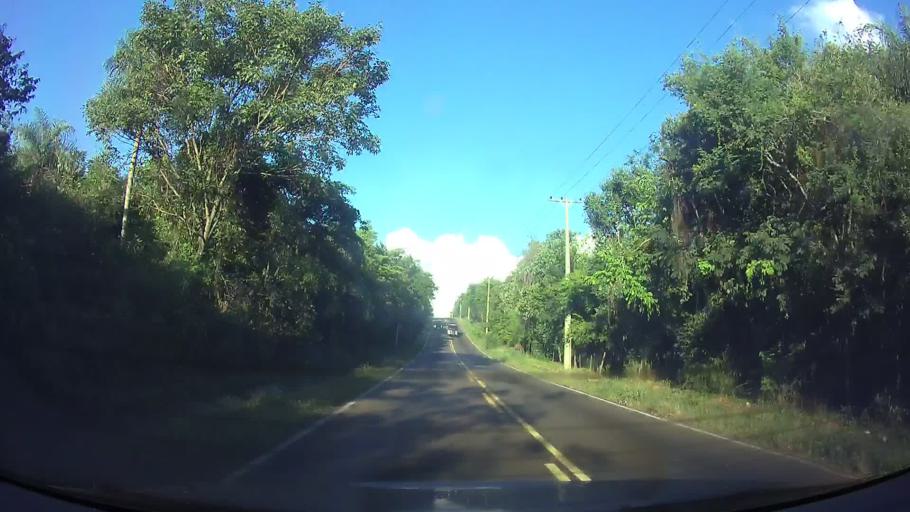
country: PY
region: Cordillera
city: Emboscada
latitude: -25.2064
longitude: -57.3486
